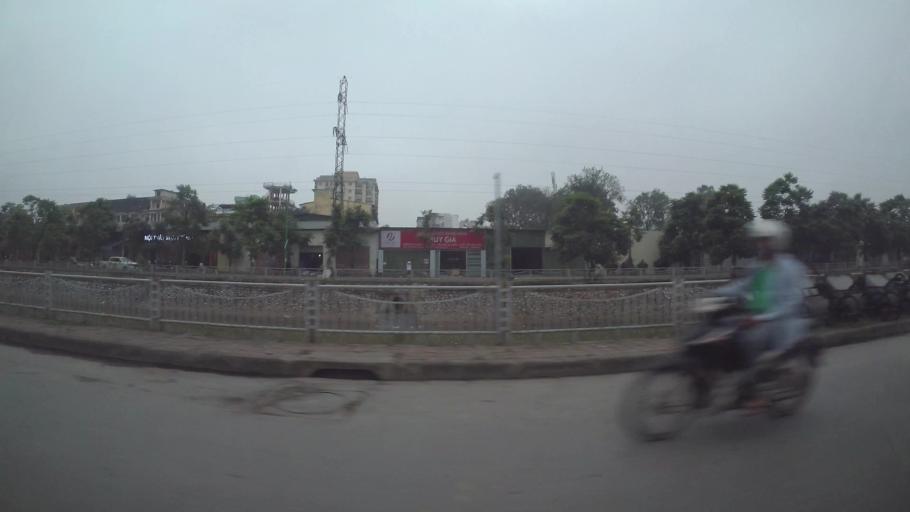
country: VN
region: Ha Noi
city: Hai BaTrung
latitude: 20.9952
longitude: 105.8364
